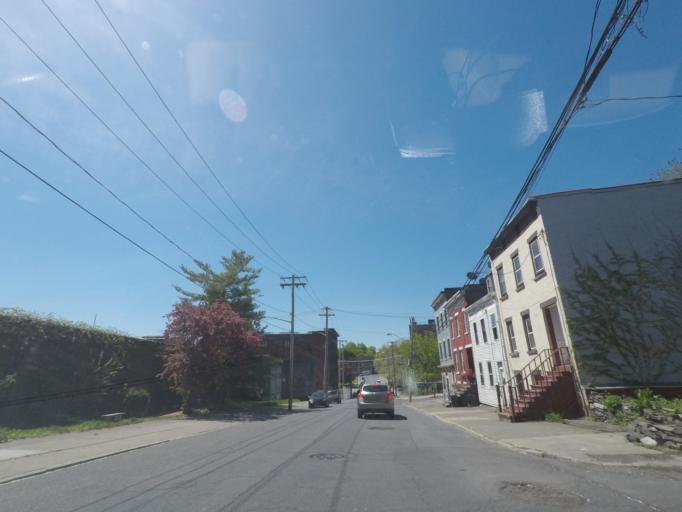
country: US
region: New York
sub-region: Albany County
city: Albany
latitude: 42.6439
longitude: -73.7581
